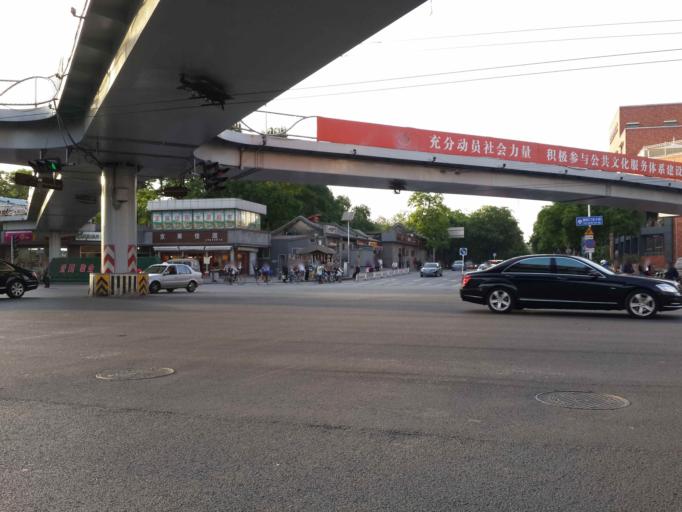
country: CN
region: Beijing
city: Chaowai
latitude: 39.9226
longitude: 116.4200
